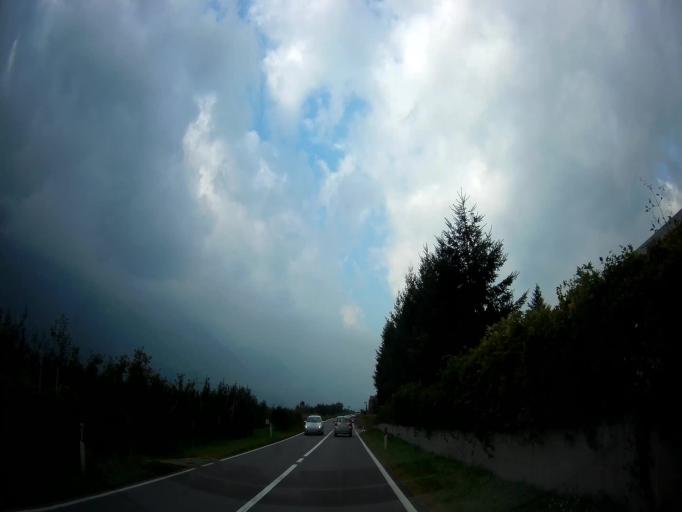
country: IT
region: Trentino-Alto Adige
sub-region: Bolzano
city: Plaus
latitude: 46.6560
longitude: 11.0271
